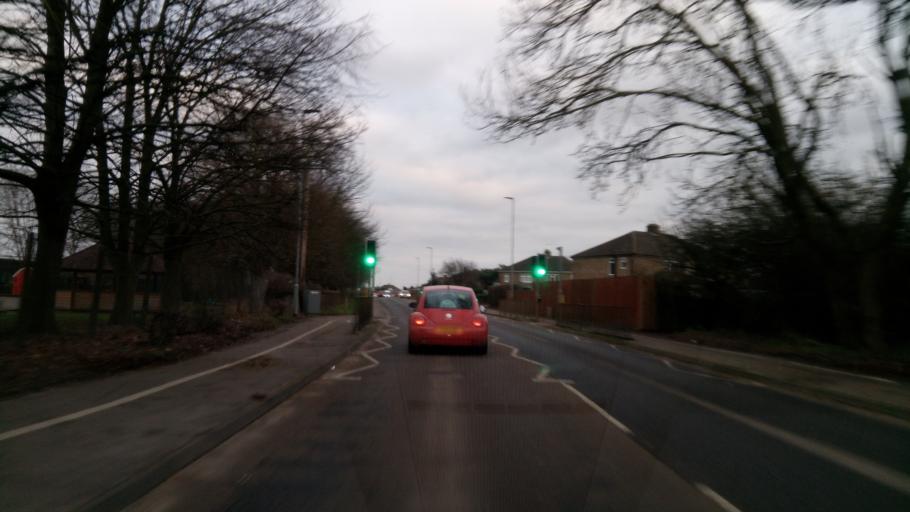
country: GB
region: England
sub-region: Peterborough
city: Peterborough
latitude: 52.5514
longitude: -0.2236
